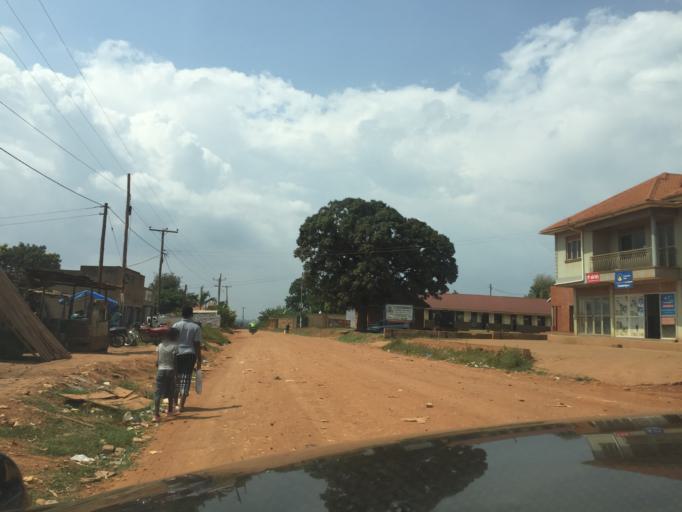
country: UG
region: Central Region
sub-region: Wakiso District
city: Kireka
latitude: 0.4046
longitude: 32.6201
